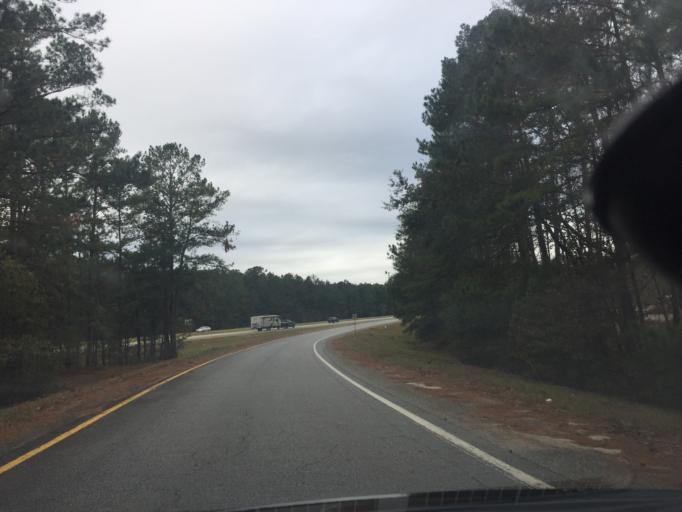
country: US
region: Georgia
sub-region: Chatham County
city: Bloomingdale
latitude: 32.1265
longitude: -81.3883
